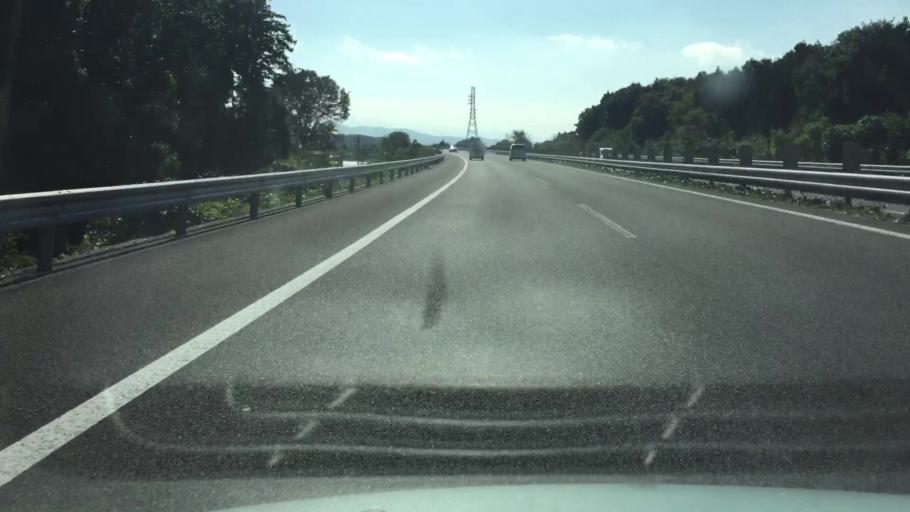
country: JP
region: Tochigi
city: Mooka
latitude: 36.4263
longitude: 139.9773
